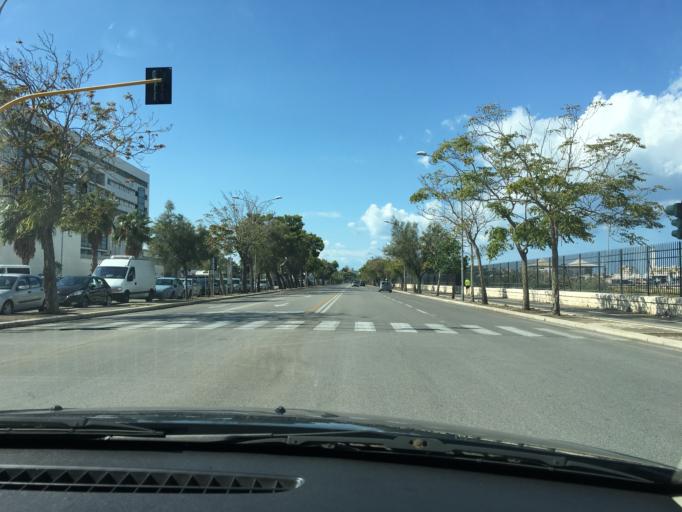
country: IT
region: Apulia
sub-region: Provincia di Bari
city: Bari
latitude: 41.1293
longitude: 16.8515
